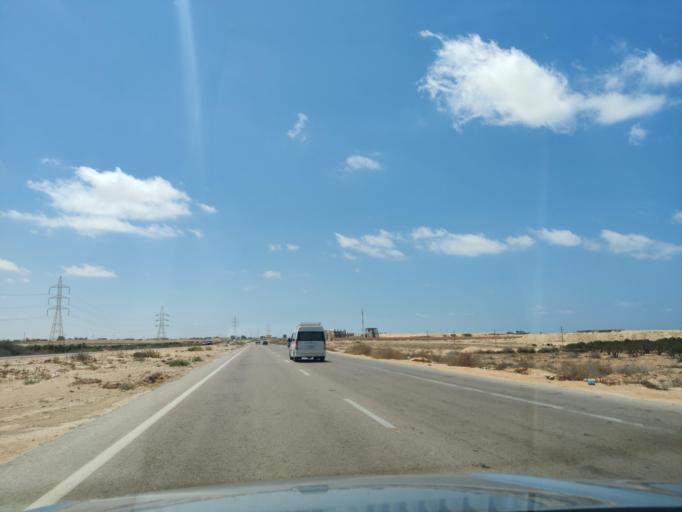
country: EG
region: Muhafazat Matruh
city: Al `Alamayn
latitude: 31.0586
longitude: 28.2114
